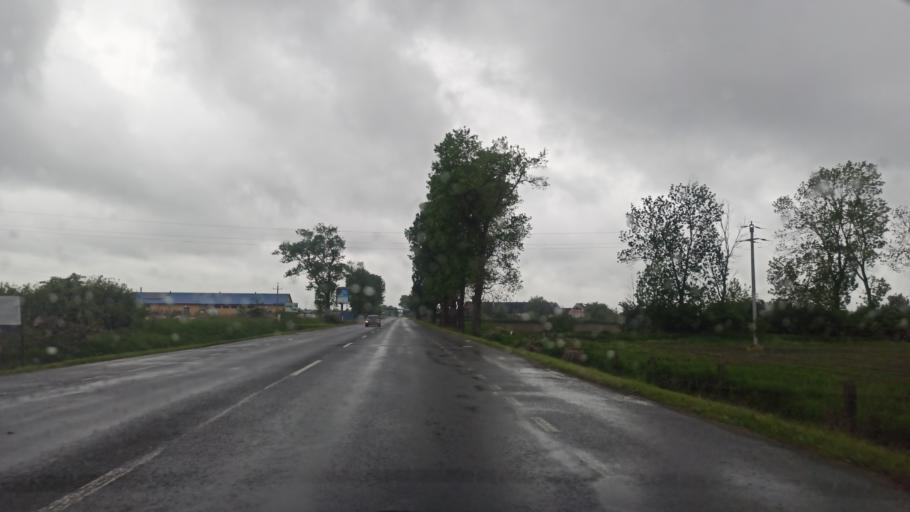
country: PL
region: Subcarpathian Voivodeship
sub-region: Powiat jaroslawski
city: Radymno
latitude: 49.9572
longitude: 22.8089
